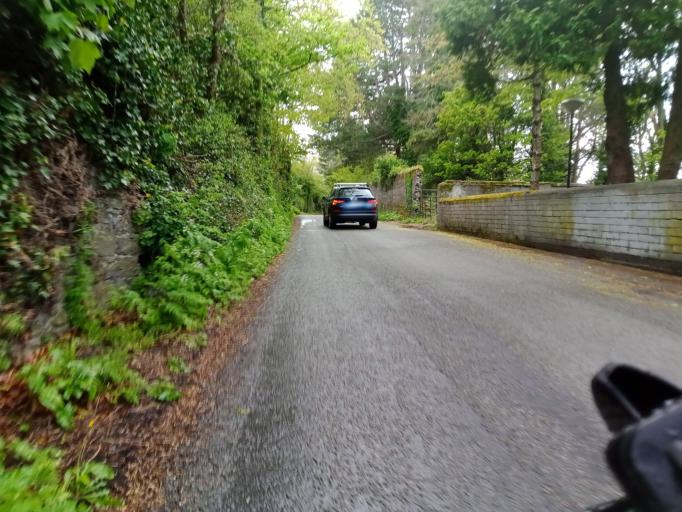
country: IE
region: Leinster
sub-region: Kilkenny
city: Kilkenny
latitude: 52.6729
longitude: -7.2587
